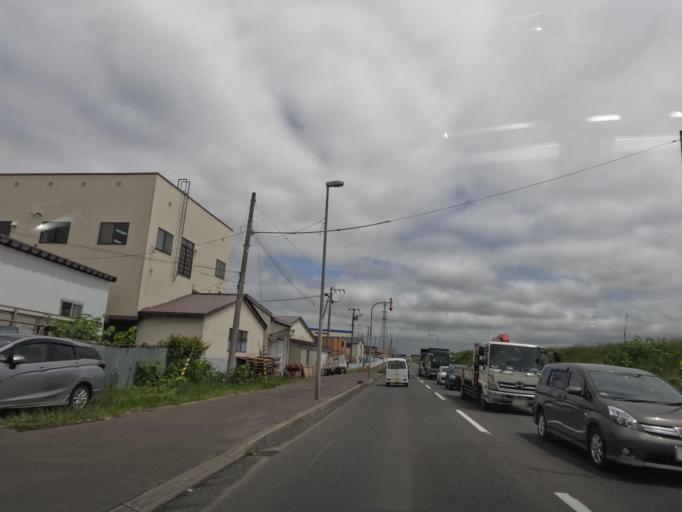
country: JP
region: Hokkaido
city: Sapporo
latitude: 43.0783
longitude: 141.4057
